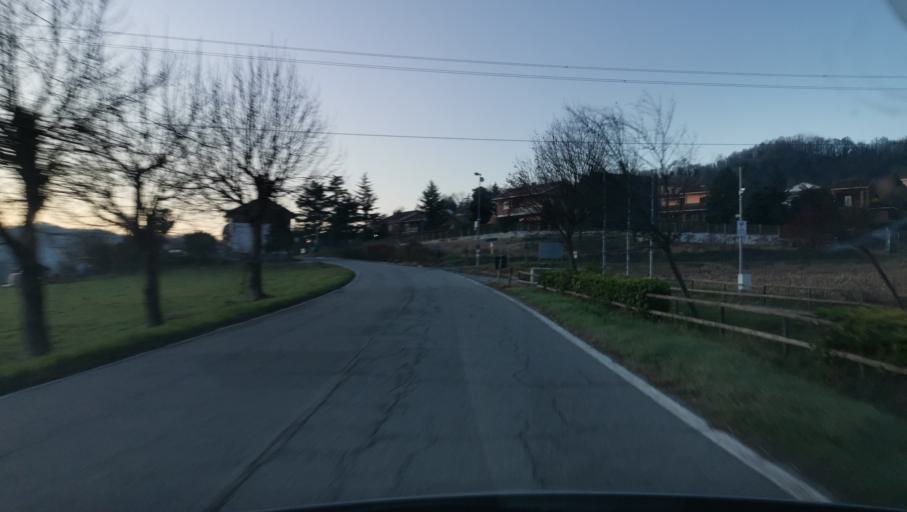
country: IT
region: Piedmont
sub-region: Provincia di Torino
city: Rivalba
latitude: 45.1136
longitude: 7.8786
